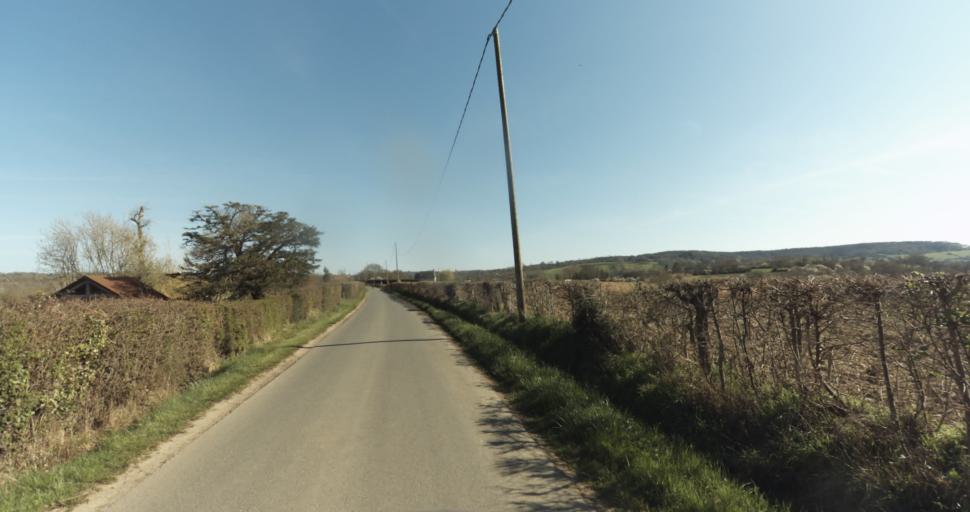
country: FR
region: Lower Normandy
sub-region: Departement du Calvados
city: Saint-Pierre-sur-Dives
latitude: 49.0329
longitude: 0.0553
